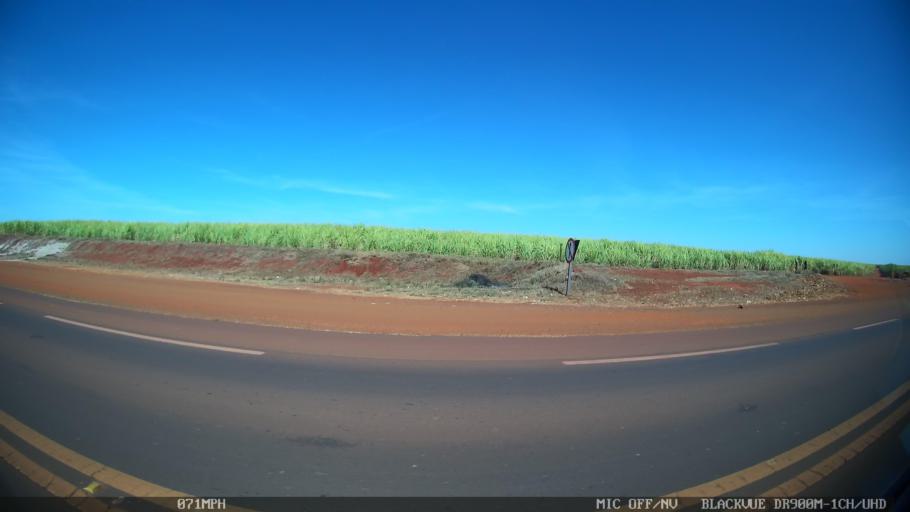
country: BR
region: Sao Paulo
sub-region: Ipua
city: Ipua
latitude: -20.4939
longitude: -48.0429
